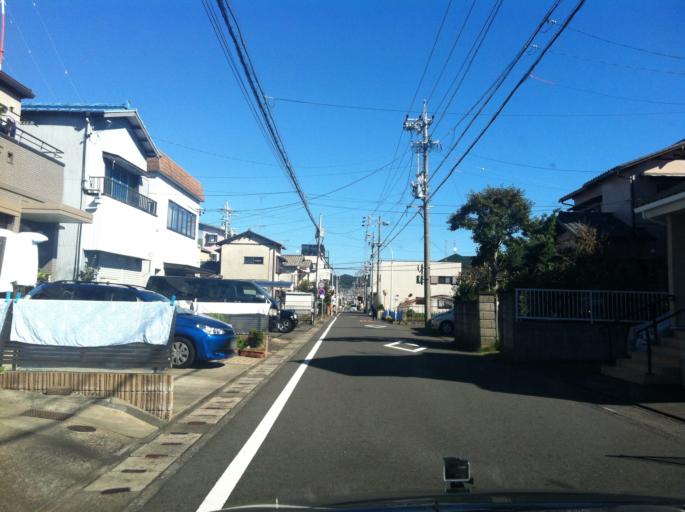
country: JP
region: Shizuoka
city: Shizuoka-shi
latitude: 34.9484
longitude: 138.4160
